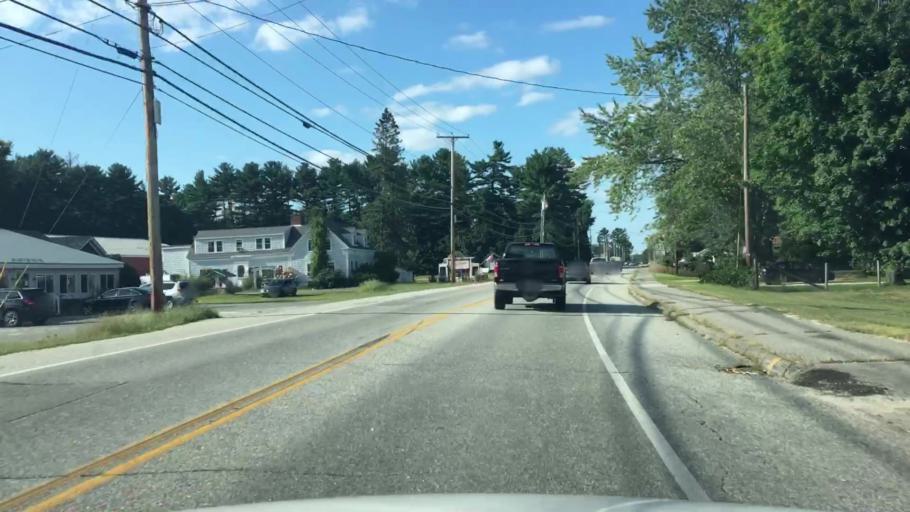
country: US
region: Maine
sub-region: Cumberland County
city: North Windham
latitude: 43.8202
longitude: -70.4339
